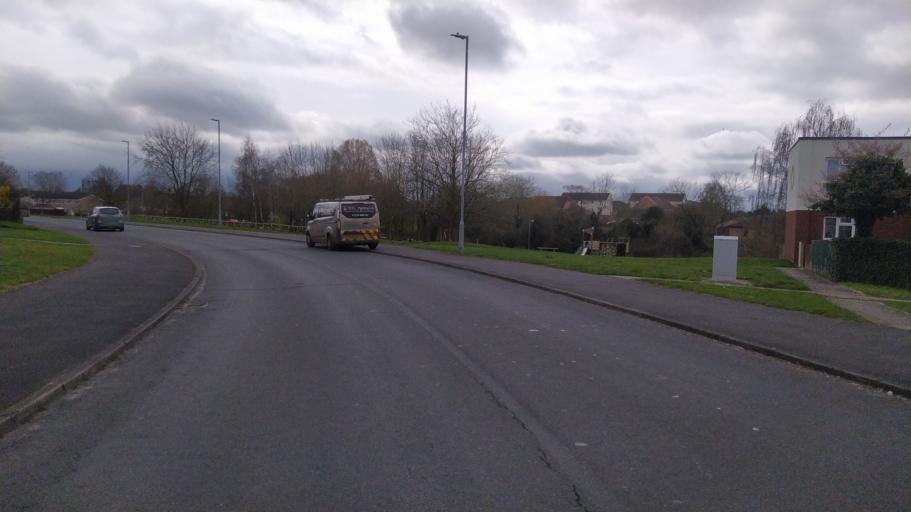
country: GB
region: England
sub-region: Wiltshire
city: Melksham
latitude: 51.3751
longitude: -2.1305
